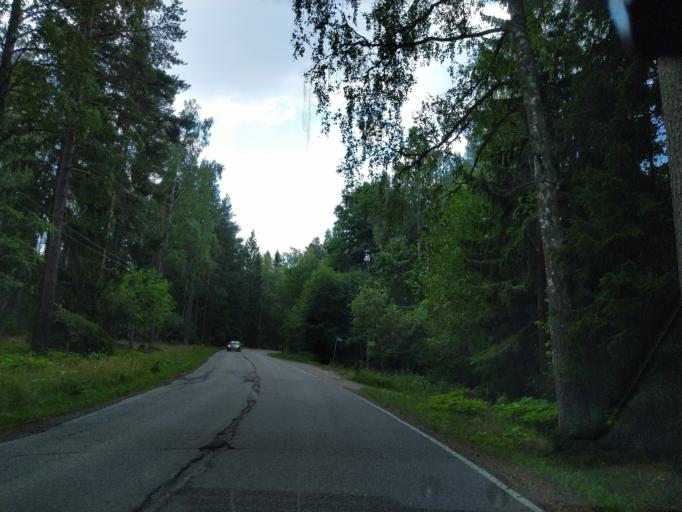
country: FI
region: Uusimaa
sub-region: Helsinki
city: Kirkkonummi
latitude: 60.0776
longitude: 24.5010
